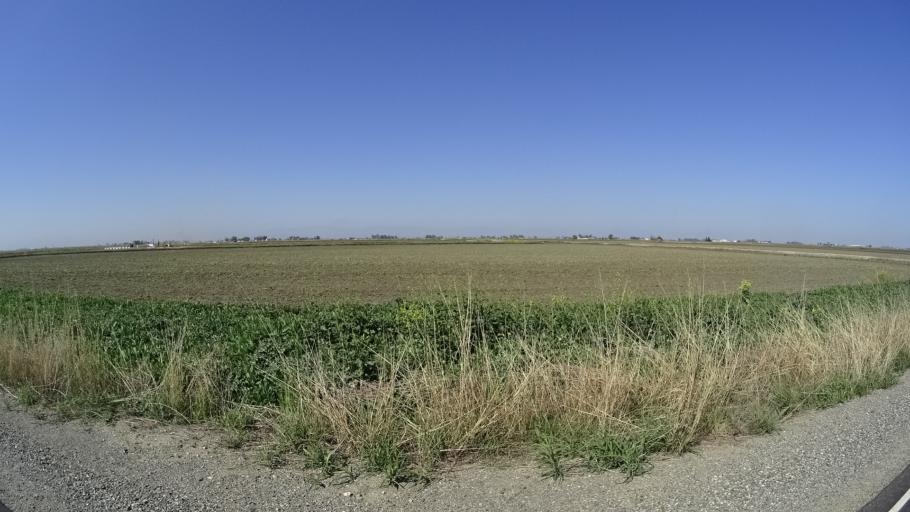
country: US
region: California
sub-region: Glenn County
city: Willows
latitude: 39.5503
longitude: -122.0652
